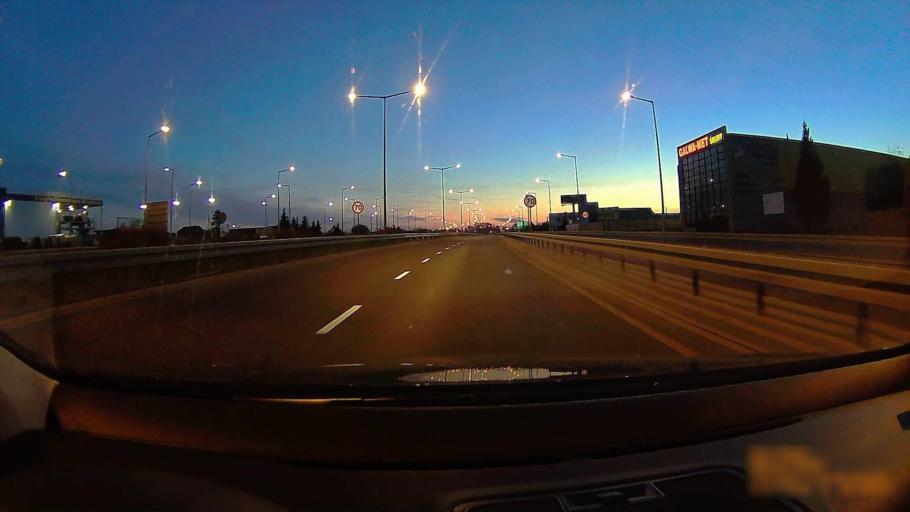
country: PL
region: Greater Poland Voivodeship
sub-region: Powiat koninski
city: Stare Miasto
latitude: 52.1856
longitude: 18.2283
